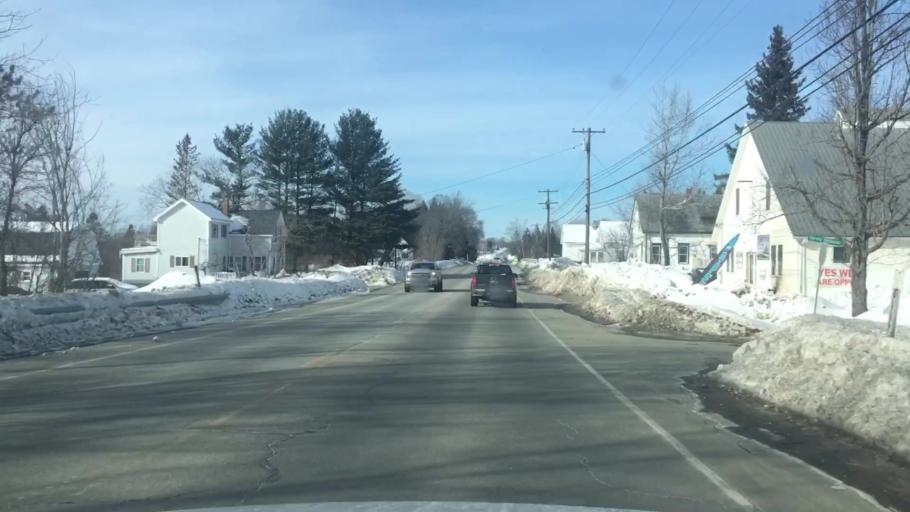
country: US
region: Maine
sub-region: Penobscot County
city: Charleston
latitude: 45.0117
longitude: -69.0265
